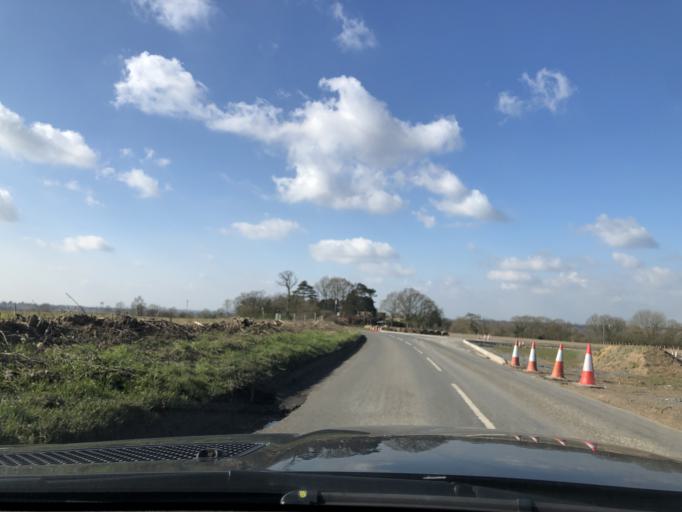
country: GB
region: England
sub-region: Warwickshire
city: Harbury
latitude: 52.2873
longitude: -1.4577
